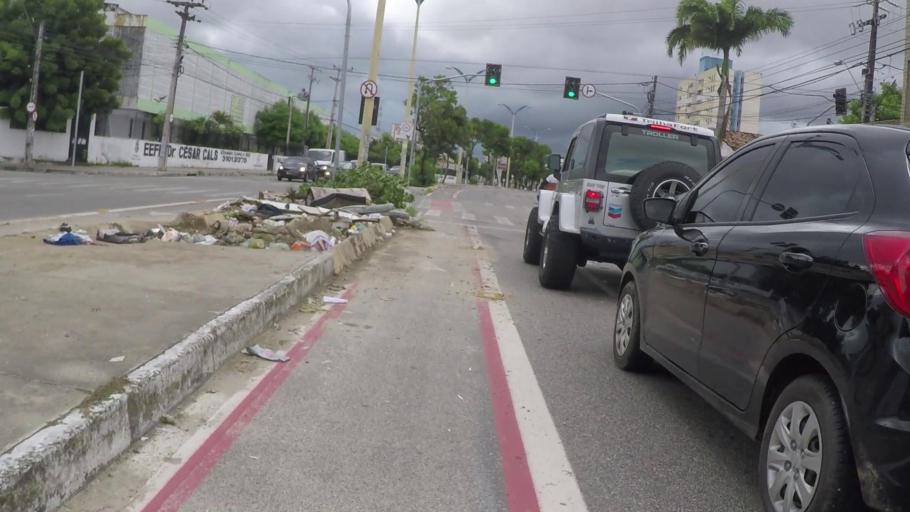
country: BR
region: Ceara
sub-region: Fortaleza
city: Fortaleza
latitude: -3.7337
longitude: -38.5401
